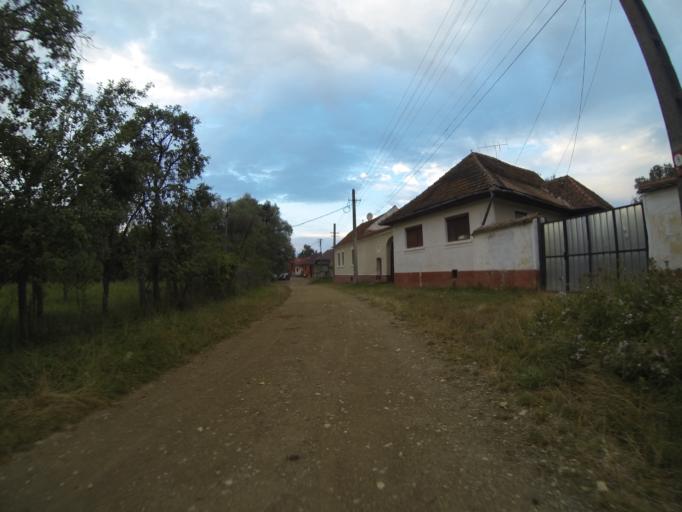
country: RO
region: Brasov
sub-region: Comuna Sinca Veche
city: Sinca Veche
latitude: 45.7629
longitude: 25.1758
